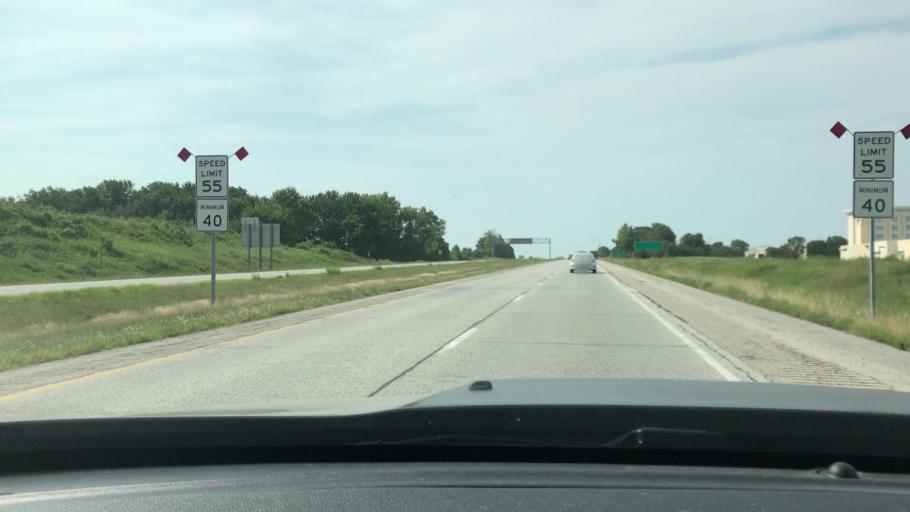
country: US
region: Iowa
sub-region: Scott County
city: Bettendorf
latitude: 41.5659
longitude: -90.5226
